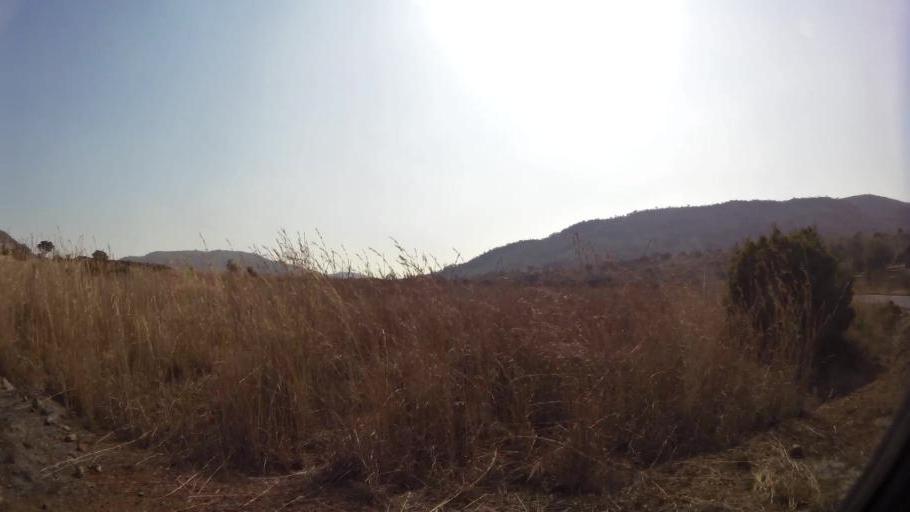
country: ZA
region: North-West
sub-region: Bojanala Platinum District Municipality
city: Mogwase
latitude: -25.3410
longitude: 27.0626
